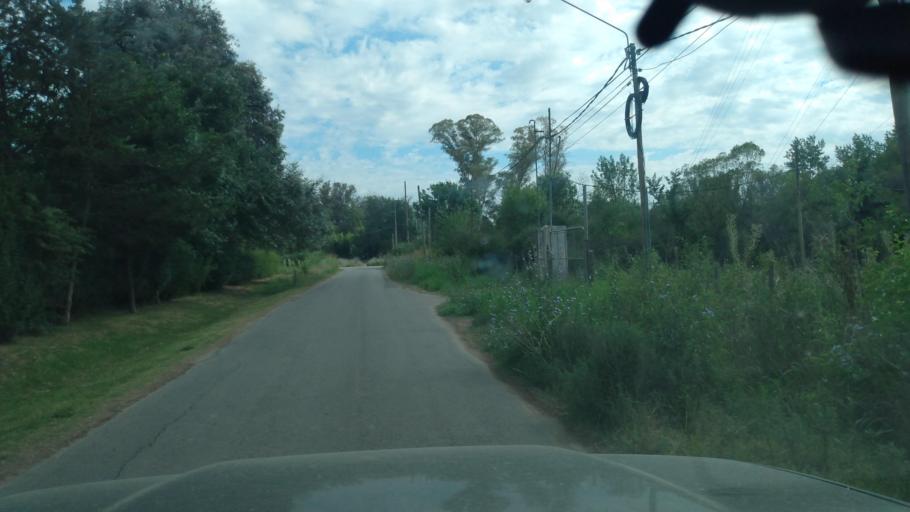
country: AR
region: Buenos Aires
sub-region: Partido de Lujan
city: Lujan
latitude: -34.5869
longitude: -59.0515
